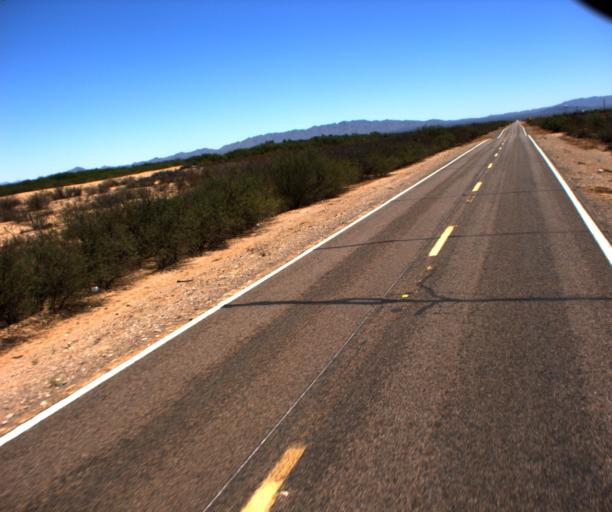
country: US
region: Arizona
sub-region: Pima County
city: Ajo
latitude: 32.1921
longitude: -112.4269
